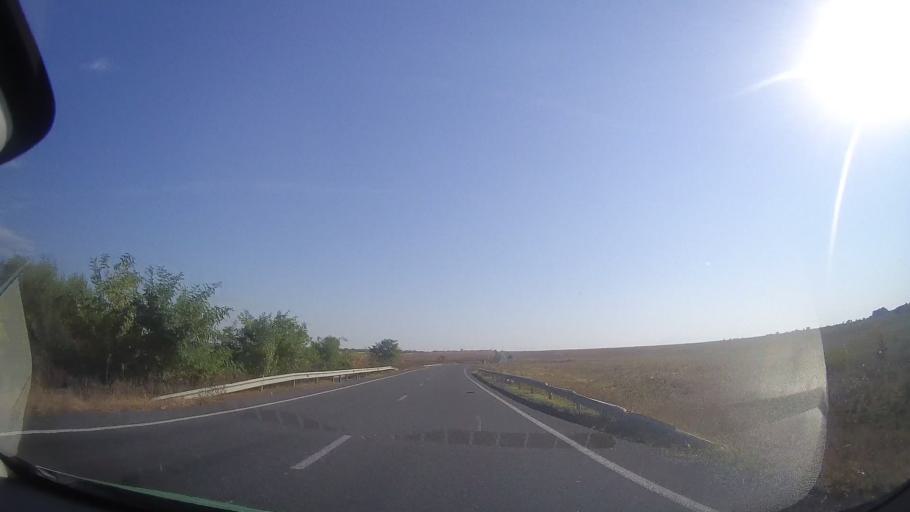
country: RO
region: Timis
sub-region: Comuna Topolovatu Mare
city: Topolovatu Mare
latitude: 45.7760
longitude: 21.6535
